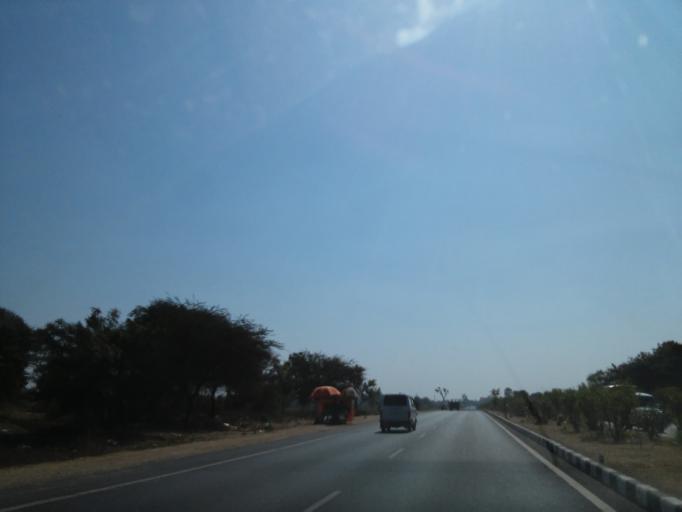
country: IN
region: Gujarat
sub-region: Mahesana
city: Vijapur
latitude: 23.4619
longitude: 72.8701
